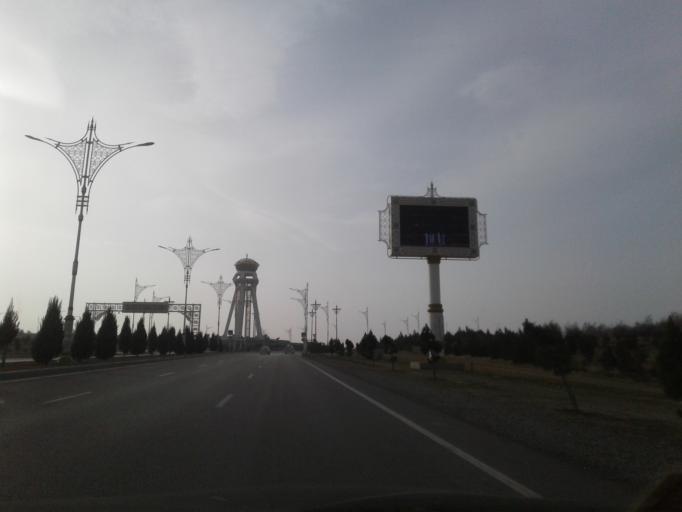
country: TM
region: Ahal
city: Ashgabat
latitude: 37.8781
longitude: 58.4252
